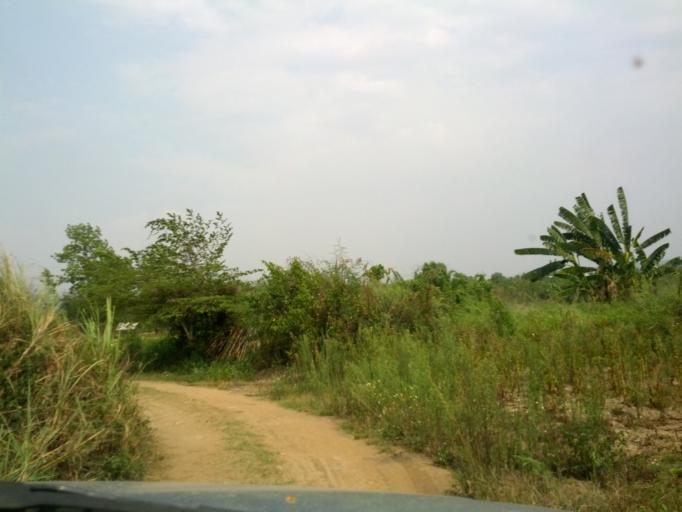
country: TH
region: Chiang Mai
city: Mae Taeng
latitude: 19.1116
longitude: 98.9902
